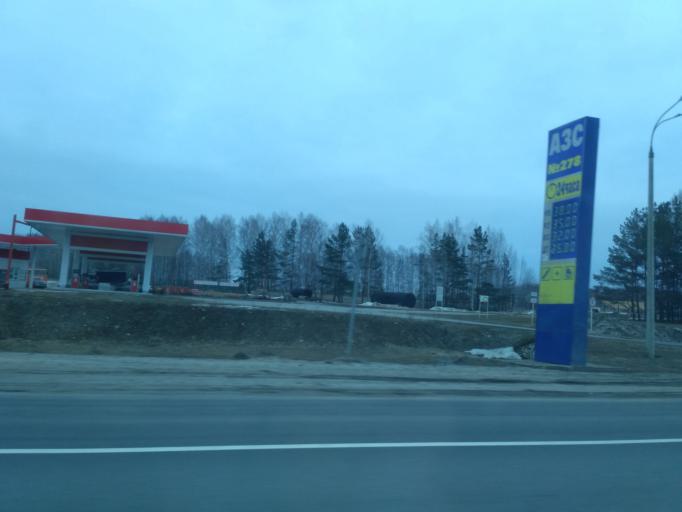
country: RU
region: Nizjnij Novgorod
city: Surovatikha
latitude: 55.7731
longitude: 44.0000
